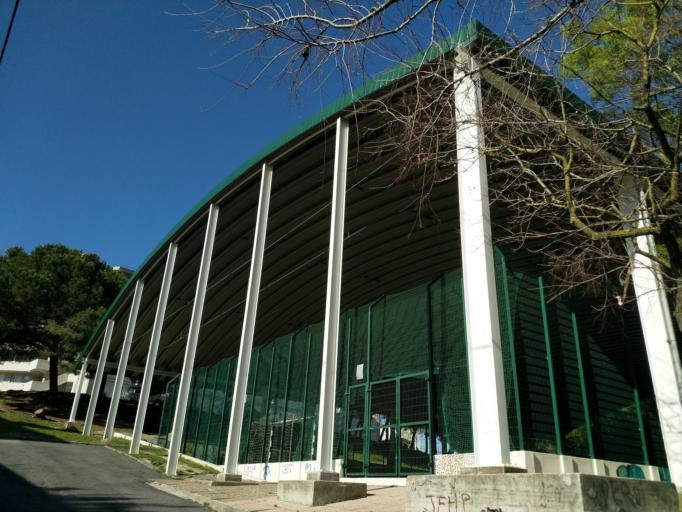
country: PT
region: Lisbon
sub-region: Loures
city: Moscavide
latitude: 38.7507
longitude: -9.1108
